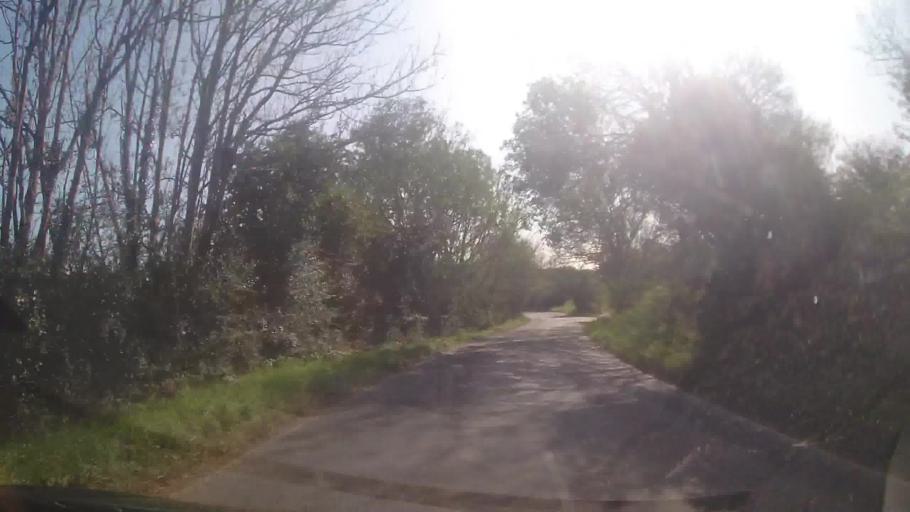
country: GB
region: Wales
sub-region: Pembrokeshire
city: Mathry
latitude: 51.9372
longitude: -5.0436
